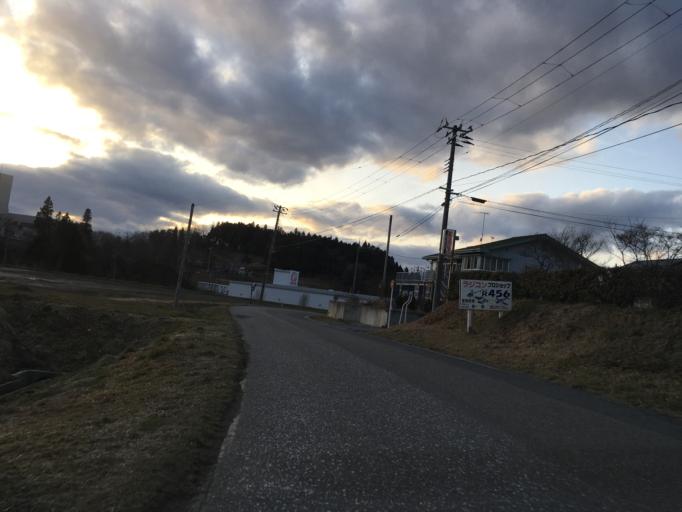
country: JP
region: Iwate
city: Ichinoseki
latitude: 38.8686
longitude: 141.3554
